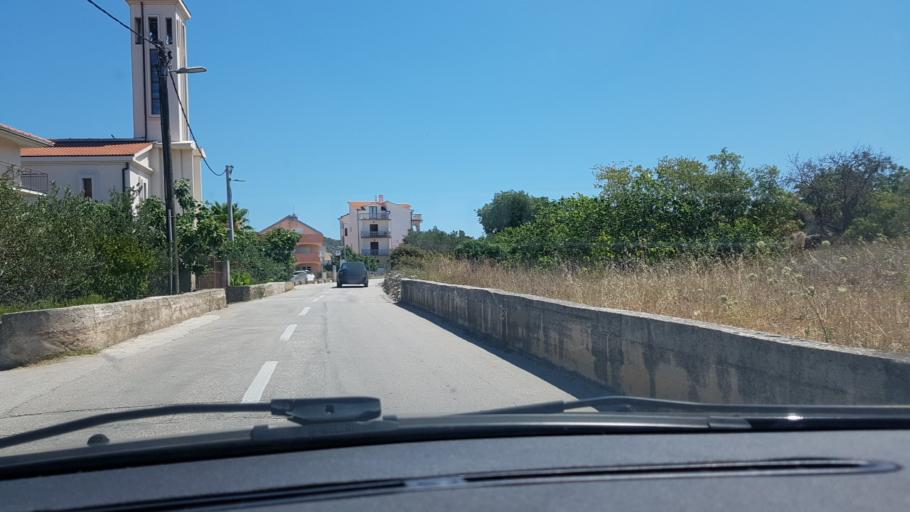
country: HR
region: Splitsko-Dalmatinska
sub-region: Grad Trogir
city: Trogir
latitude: 43.4924
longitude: 16.2640
